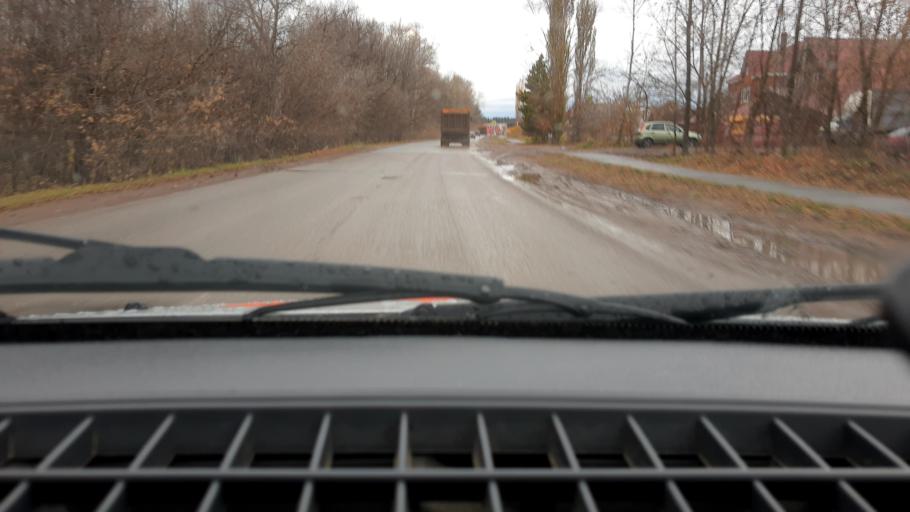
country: RU
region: Bashkortostan
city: Ufa
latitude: 54.7926
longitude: 55.9562
